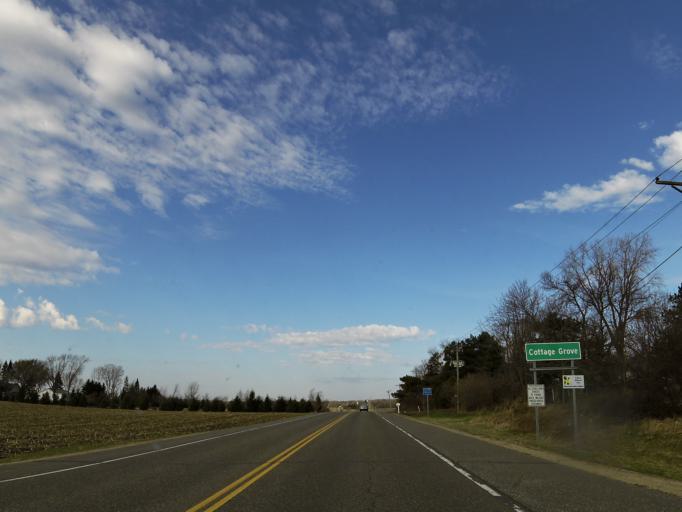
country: US
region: Minnesota
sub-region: Washington County
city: Cottage Grove
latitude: 44.8479
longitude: -92.8637
